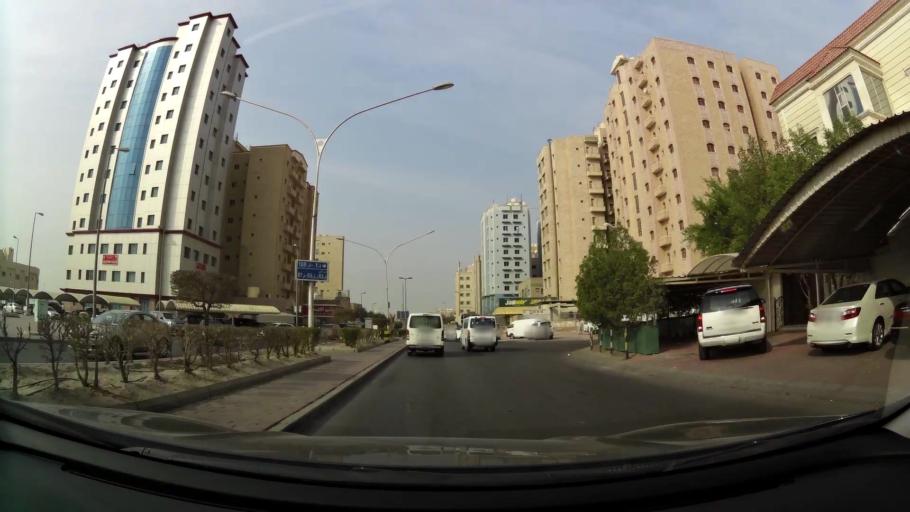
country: KW
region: Al Farwaniyah
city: Al Farwaniyah
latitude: 29.2869
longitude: 47.9551
